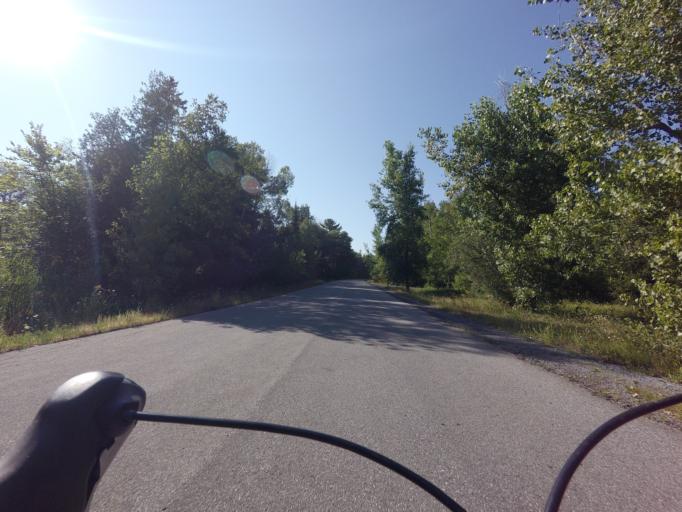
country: CA
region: Ontario
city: Bells Corners
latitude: 45.4877
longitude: -76.0439
